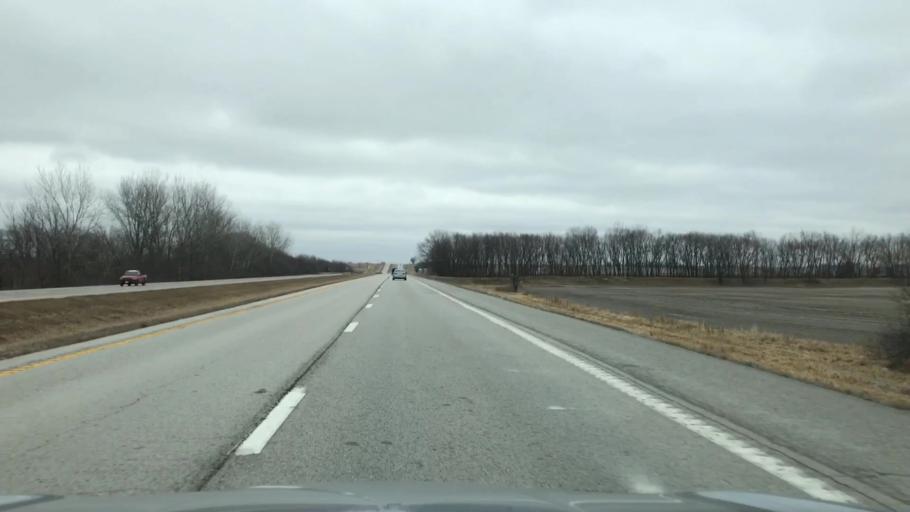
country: US
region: Missouri
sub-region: Livingston County
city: Chillicothe
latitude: 39.7768
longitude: -93.4200
